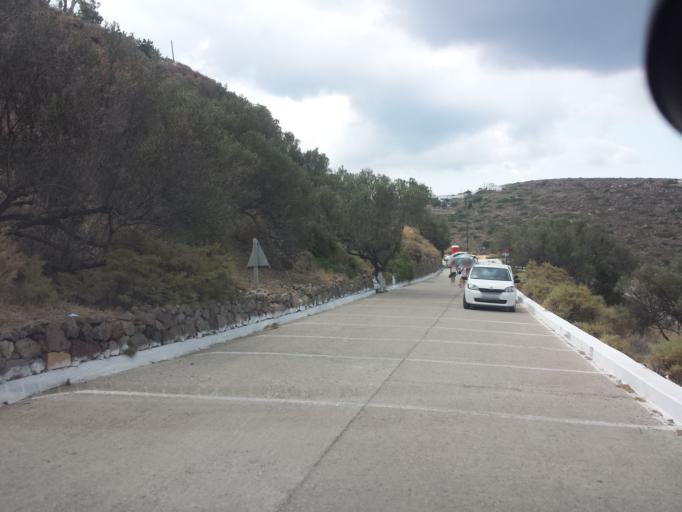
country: GR
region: South Aegean
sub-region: Nomos Kykladon
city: Milos
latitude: 36.7386
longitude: 24.4231
